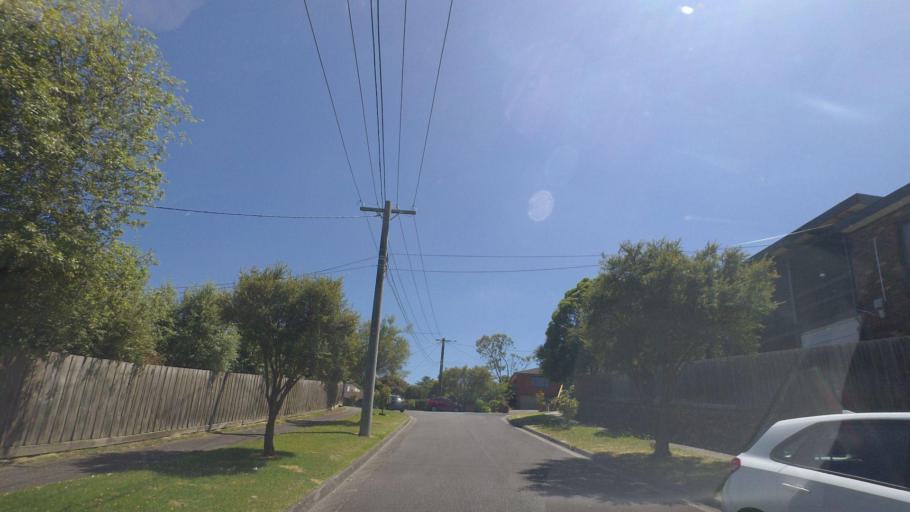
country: AU
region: Victoria
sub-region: Knox
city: Ferntree Gully
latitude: -37.8988
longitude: 145.2870
